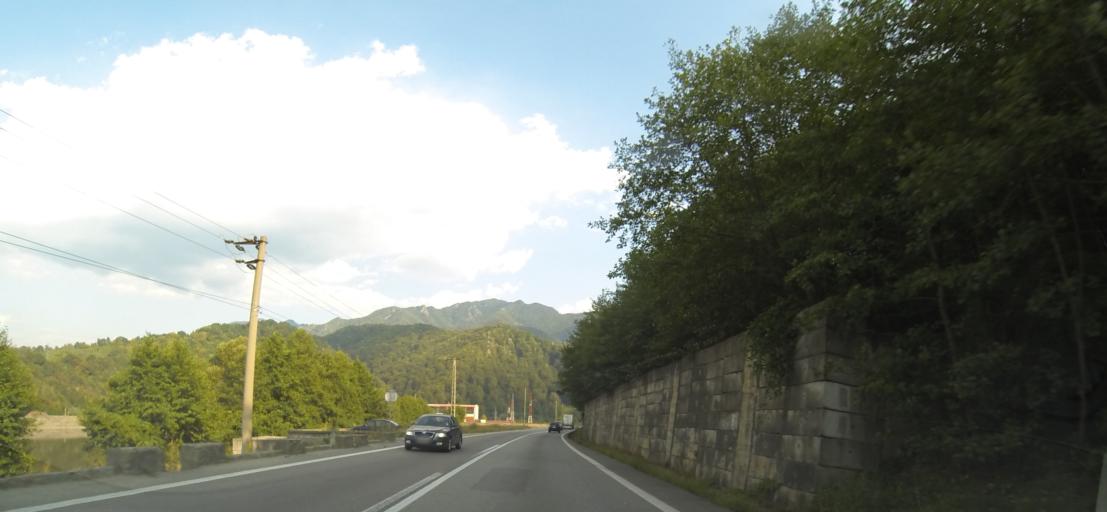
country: RO
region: Valcea
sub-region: Comuna Brezoi
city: Brezoi
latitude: 45.3460
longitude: 24.2711
